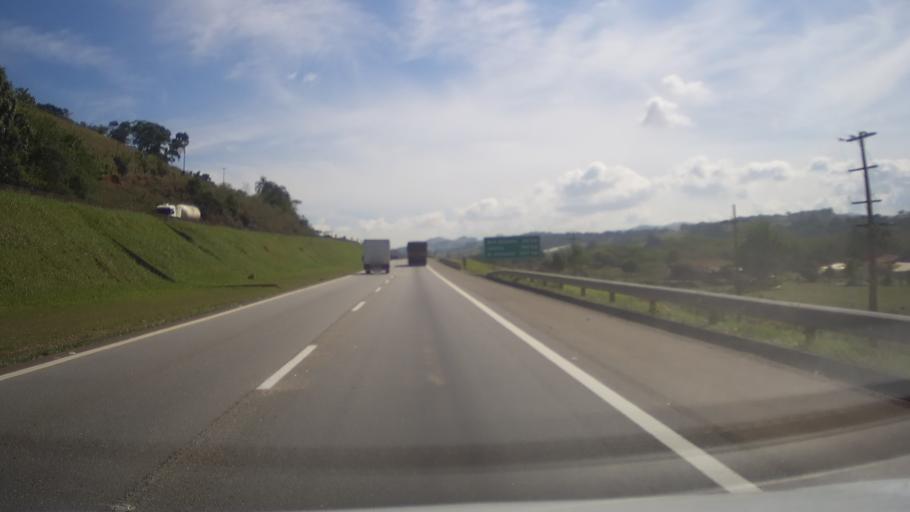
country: BR
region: Minas Gerais
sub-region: Cambui
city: Cambui
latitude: -22.5845
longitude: -46.0480
